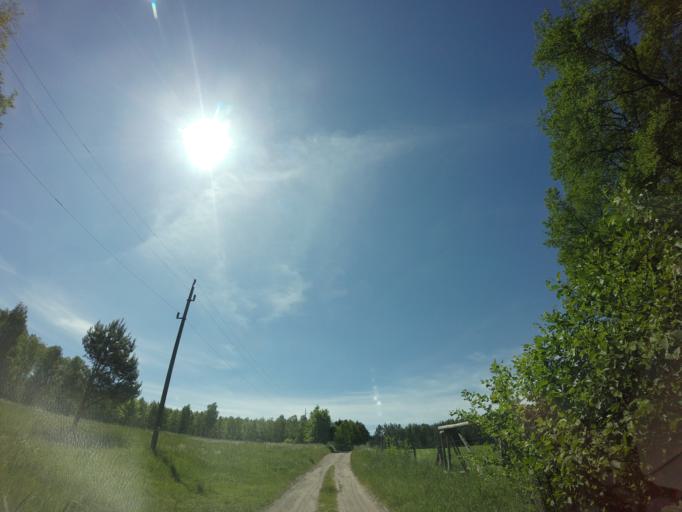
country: PL
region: West Pomeranian Voivodeship
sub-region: Powiat choszczenski
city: Drawno
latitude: 53.2964
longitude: 15.6912
